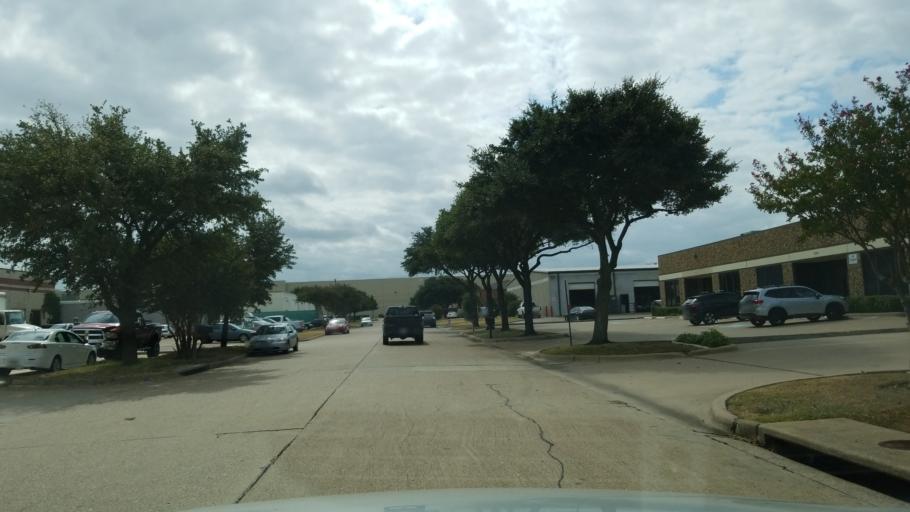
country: US
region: Texas
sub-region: Dallas County
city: Garland
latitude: 32.8886
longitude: -96.6815
